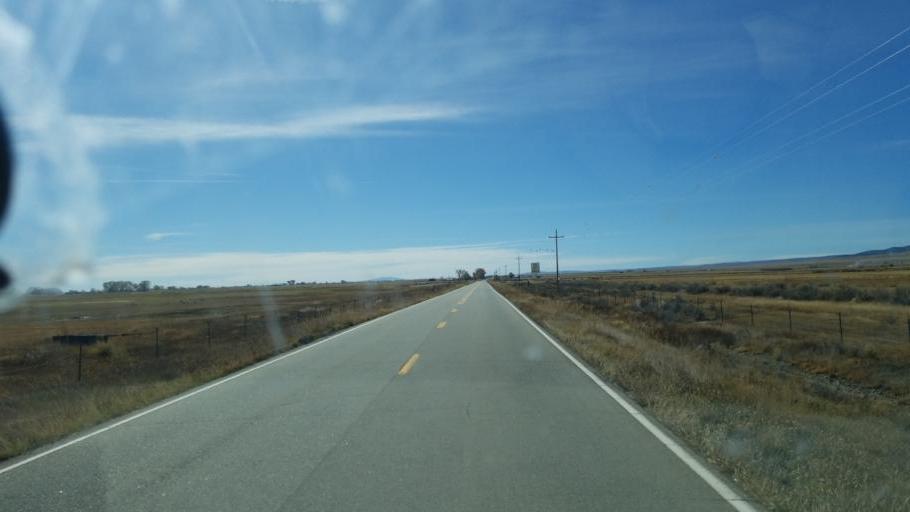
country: US
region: Colorado
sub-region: Rio Grande County
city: Monte Vista
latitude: 37.4713
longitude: -106.1487
